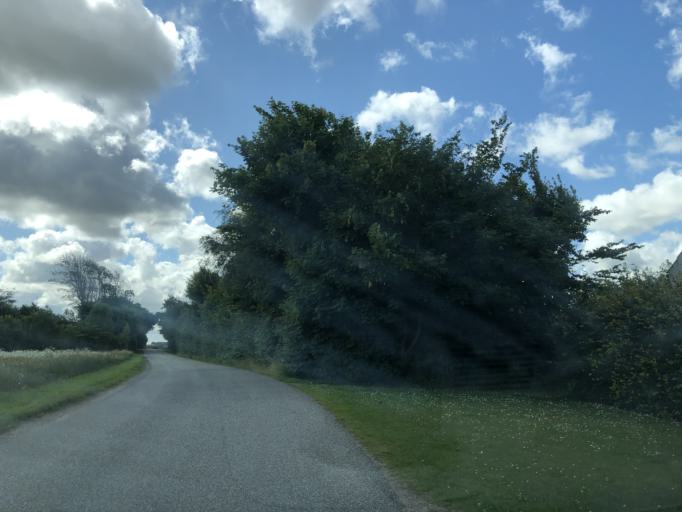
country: DK
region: Central Jutland
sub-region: Struer Kommune
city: Struer
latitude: 56.4600
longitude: 8.5224
